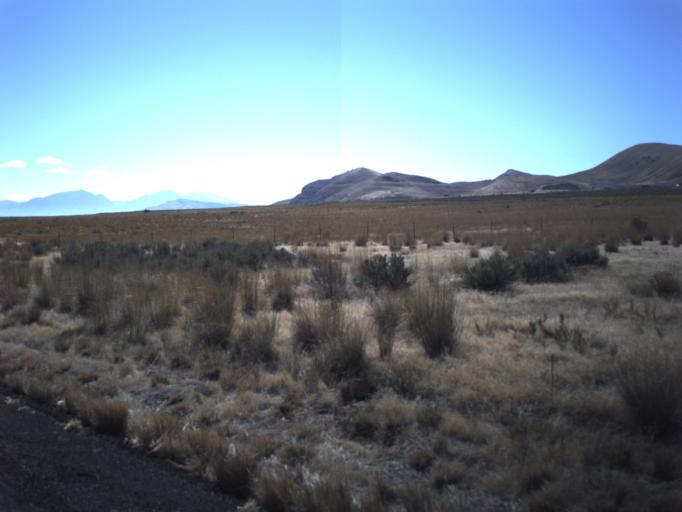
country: US
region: Utah
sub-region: Utah County
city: Saratoga Springs
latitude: 40.2864
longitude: -111.8753
